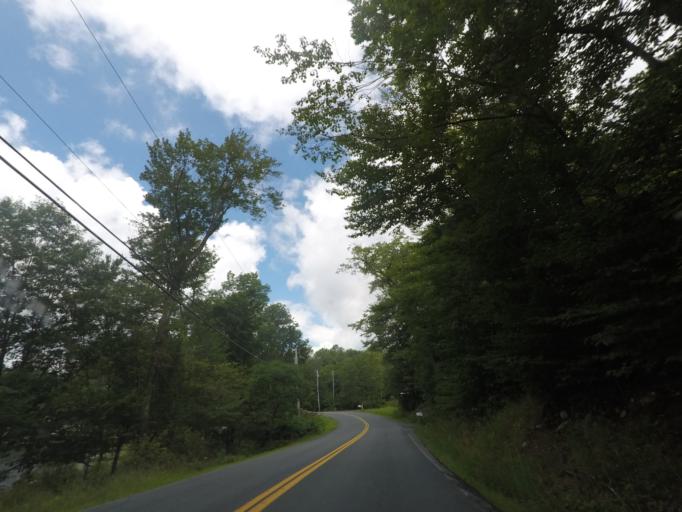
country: US
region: New York
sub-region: Rensselaer County
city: Averill Park
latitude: 42.6455
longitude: -73.4822
